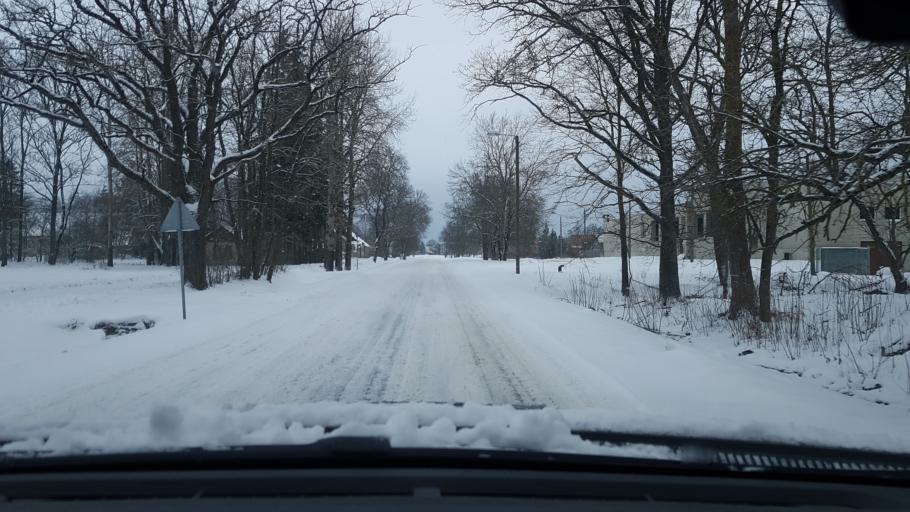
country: EE
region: Harju
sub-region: Kuusalu vald
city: Kuusalu
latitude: 59.4482
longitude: 25.3842
